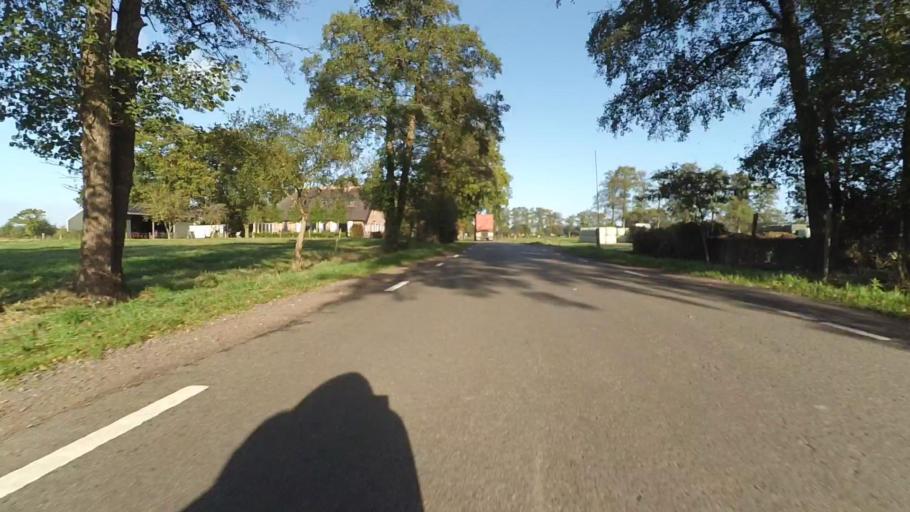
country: NL
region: Gelderland
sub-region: Gemeente Ermelo
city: Horst
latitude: 52.2897
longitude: 5.5655
